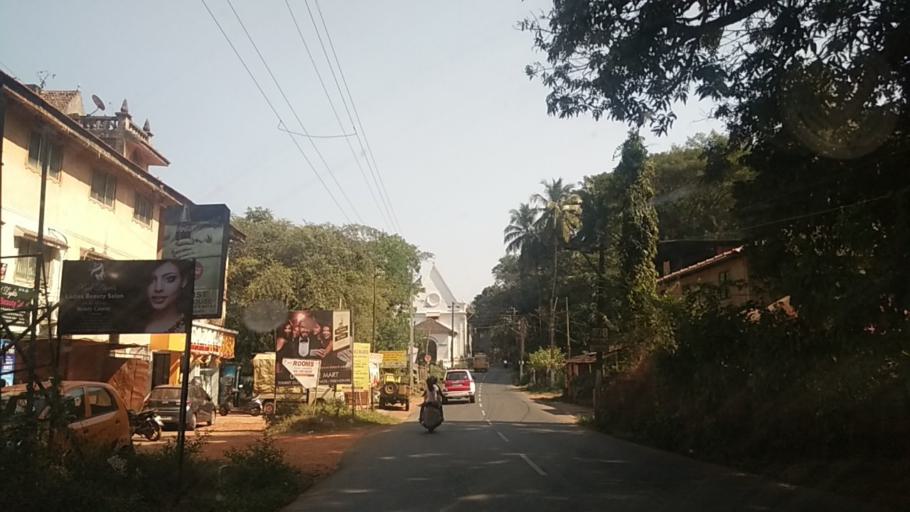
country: IN
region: Goa
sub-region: North Goa
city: Bambolim
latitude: 15.5002
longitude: 73.8957
